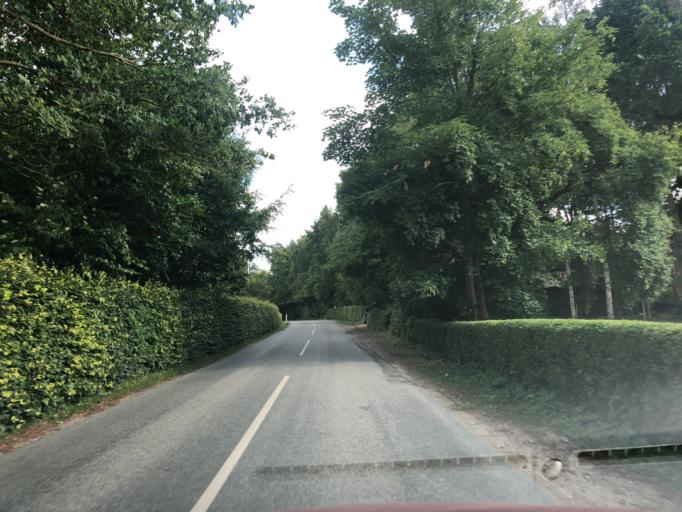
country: DK
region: Zealand
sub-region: Stevns Kommune
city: Harlev
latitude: 55.2838
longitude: 12.2214
